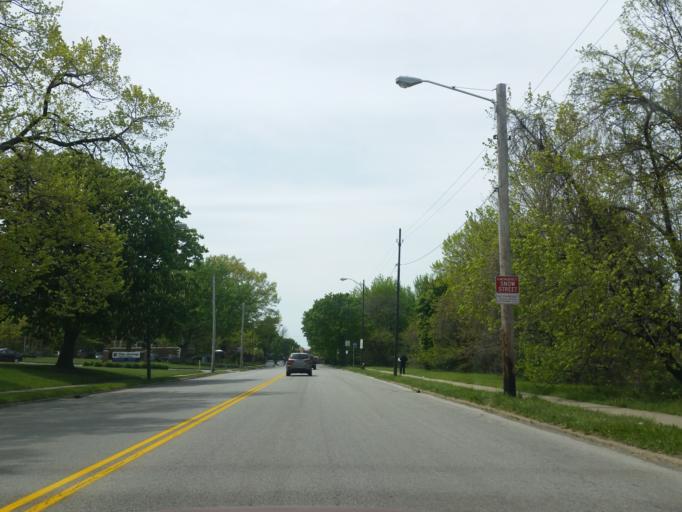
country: US
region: Ohio
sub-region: Cuyahoga County
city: Lakewood
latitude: 41.4813
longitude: -81.7594
